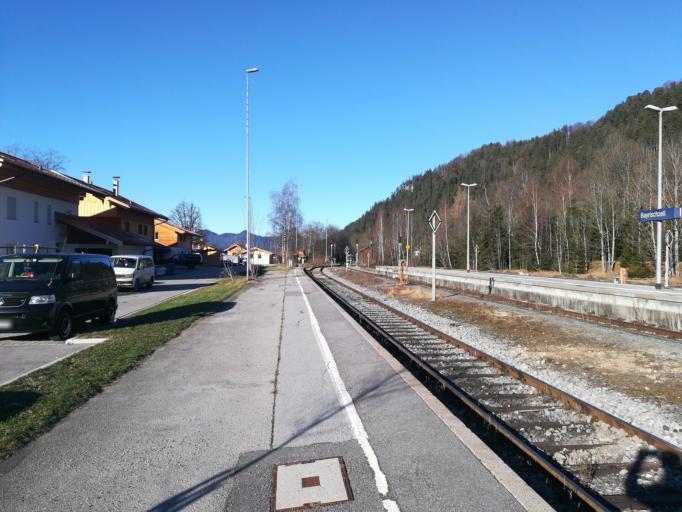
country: DE
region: Bavaria
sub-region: Upper Bavaria
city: Bayrischzell
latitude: 47.6755
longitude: 12.0111
